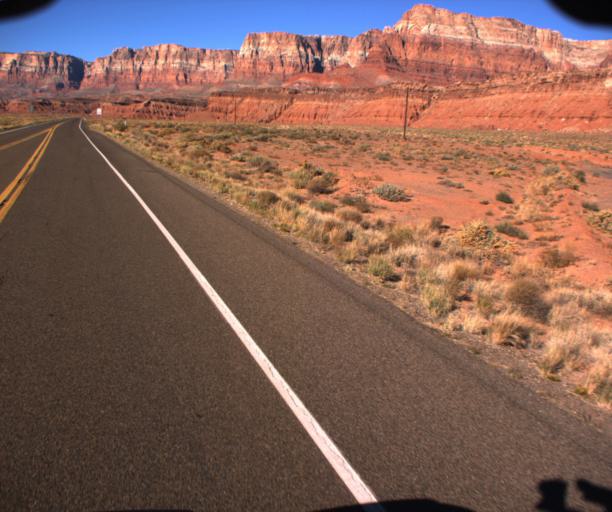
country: US
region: Arizona
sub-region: Coconino County
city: Page
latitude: 36.8161
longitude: -111.6389
